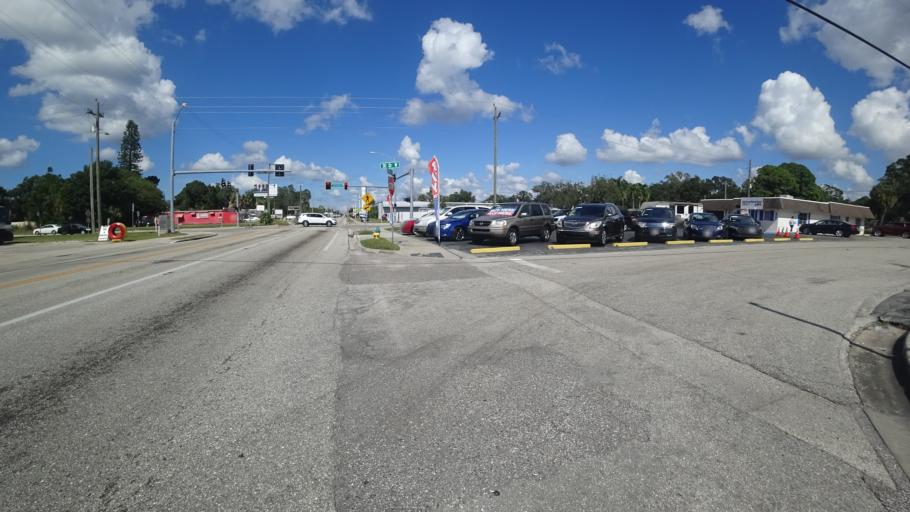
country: US
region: Florida
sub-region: Manatee County
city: South Bradenton
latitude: 27.4734
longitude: -82.5712
